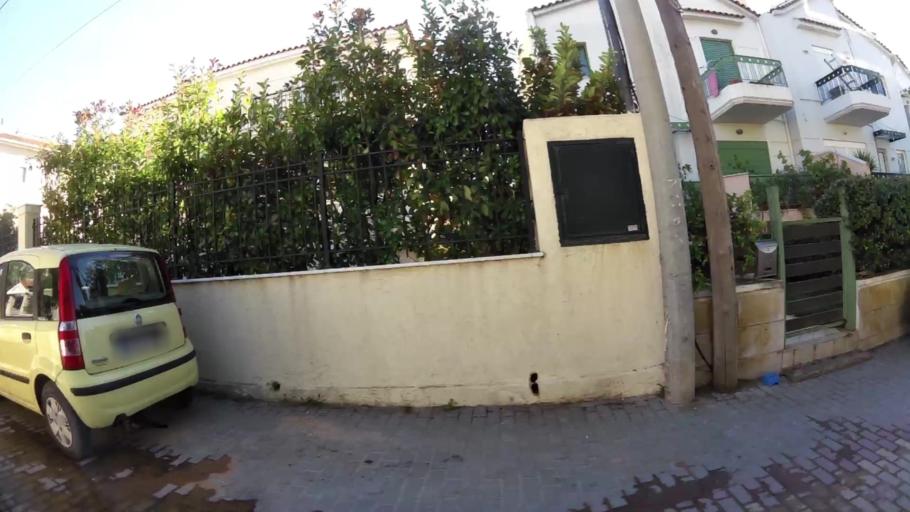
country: GR
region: Attica
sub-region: Nomarchia Athinas
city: Nea Erythraia
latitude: 38.0973
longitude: 23.8172
